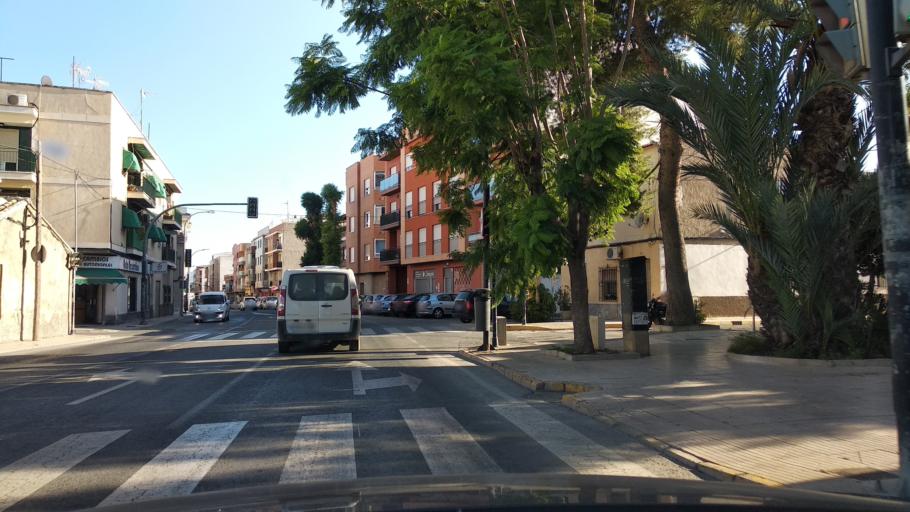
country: ES
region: Murcia
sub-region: Murcia
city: Santomera
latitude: 38.0624
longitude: -1.0537
